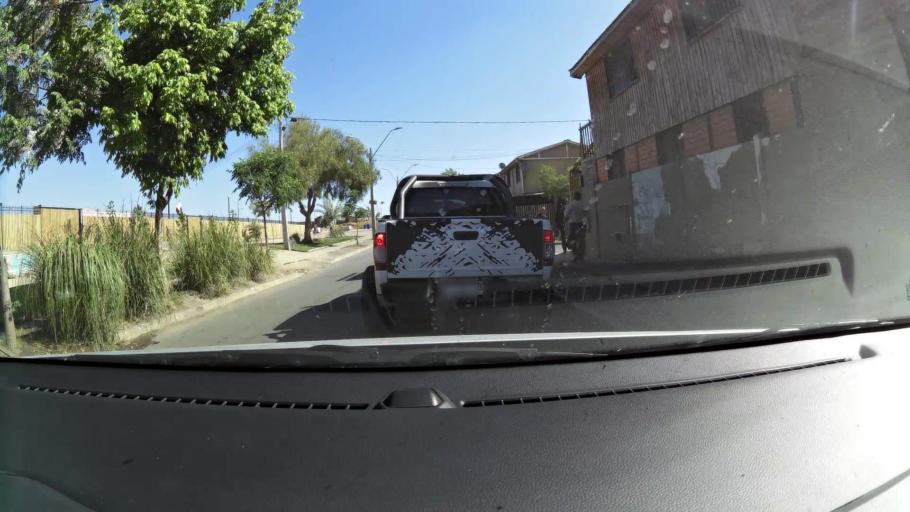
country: CL
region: Santiago Metropolitan
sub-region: Provincia de Maipo
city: San Bernardo
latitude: -33.5910
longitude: -70.6674
